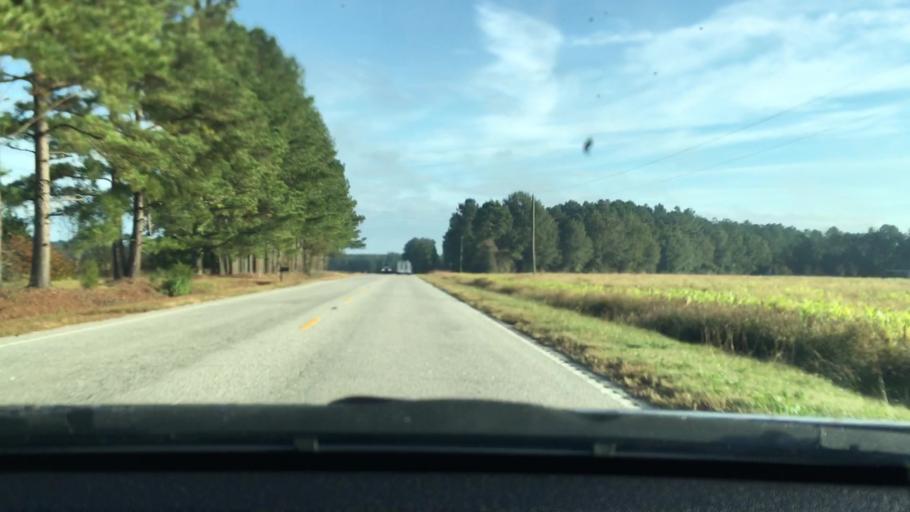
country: US
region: South Carolina
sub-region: Sumter County
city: East Sumter
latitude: 34.0248
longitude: -80.2765
